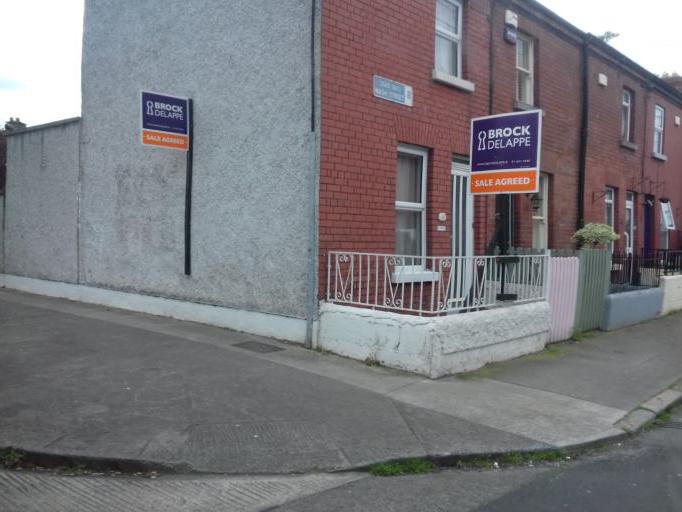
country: IE
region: Leinster
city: Crumlin
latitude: 53.3361
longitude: -6.3299
